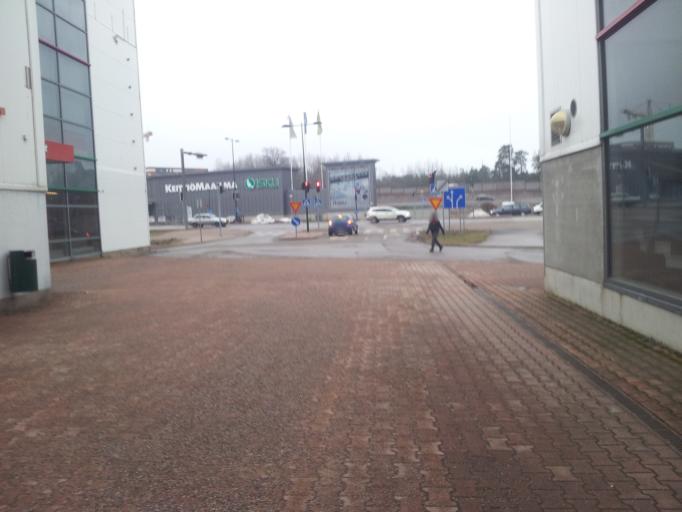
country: FI
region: Uusimaa
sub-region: Helsinki
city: Koukkuniemi
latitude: 60.1628
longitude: 24.7179
